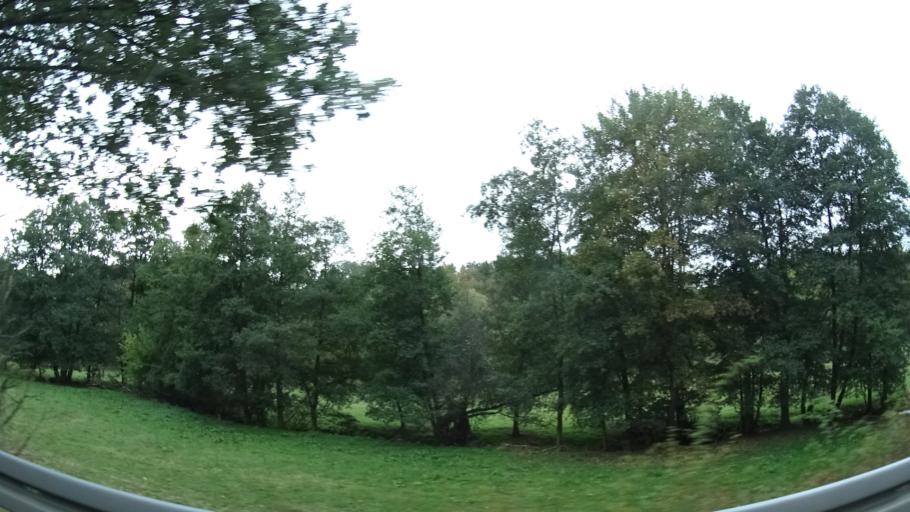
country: DE
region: Thuringia
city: Wahns
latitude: 50.6330
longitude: 10.2887
